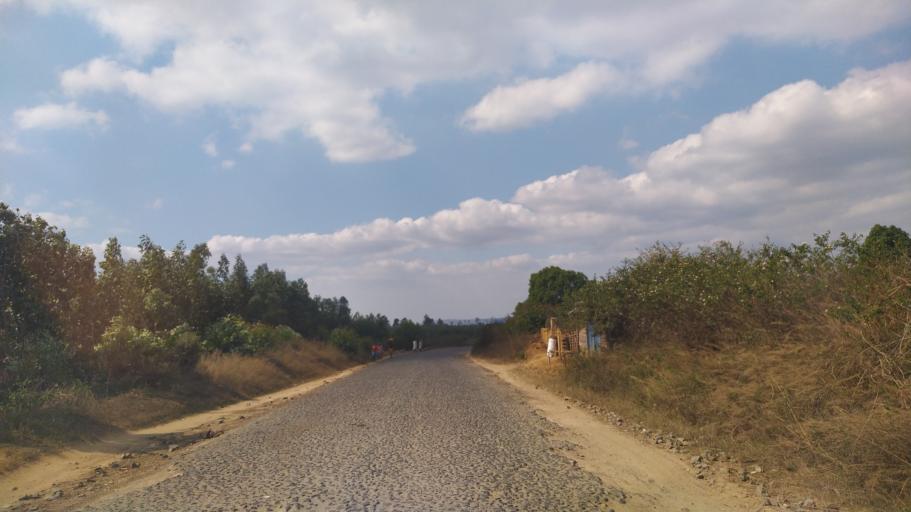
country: MG
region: Alaotra Mangoro
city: Moramanga
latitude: -18.7694
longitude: 48.2516
